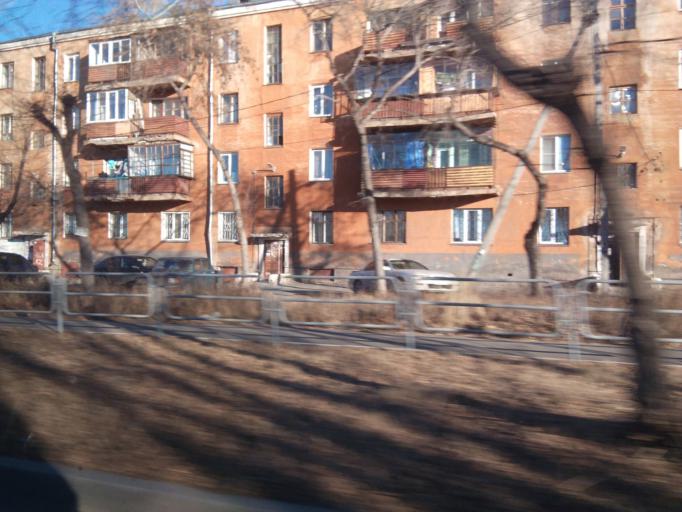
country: RU
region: Chelyabinsk
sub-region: Gorod Magnitogorsk
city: Magnitogorsk
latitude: 53.3903
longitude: 59.0521
